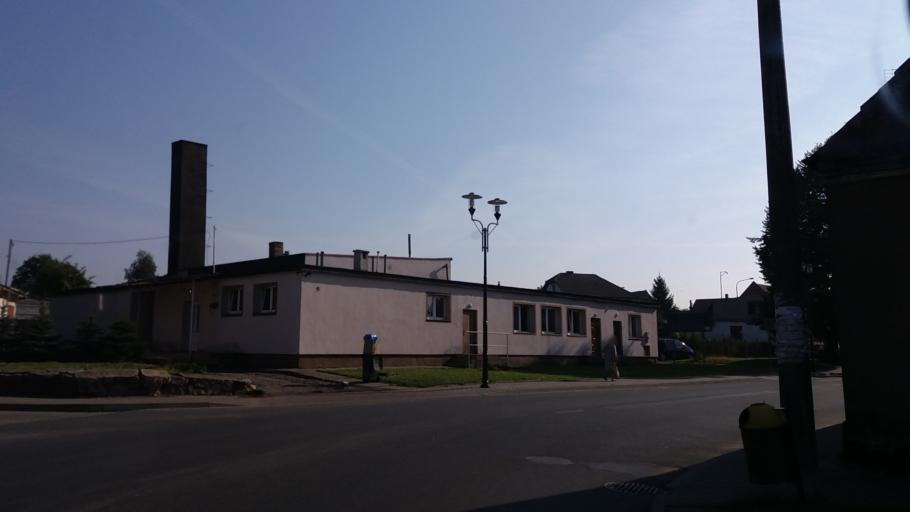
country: PL
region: West Pomeranian Voivodeship
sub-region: Powiat choszczenski
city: Pelczyce
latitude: 53.0431
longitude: 15.3050
